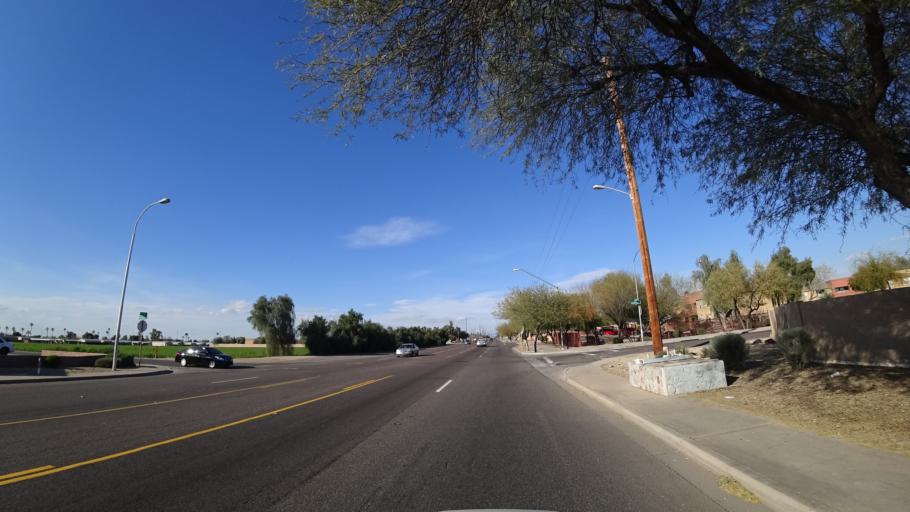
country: US
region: Arizona
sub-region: Maricopa County
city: Peoria
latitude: 33.5337
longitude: -112.2376
